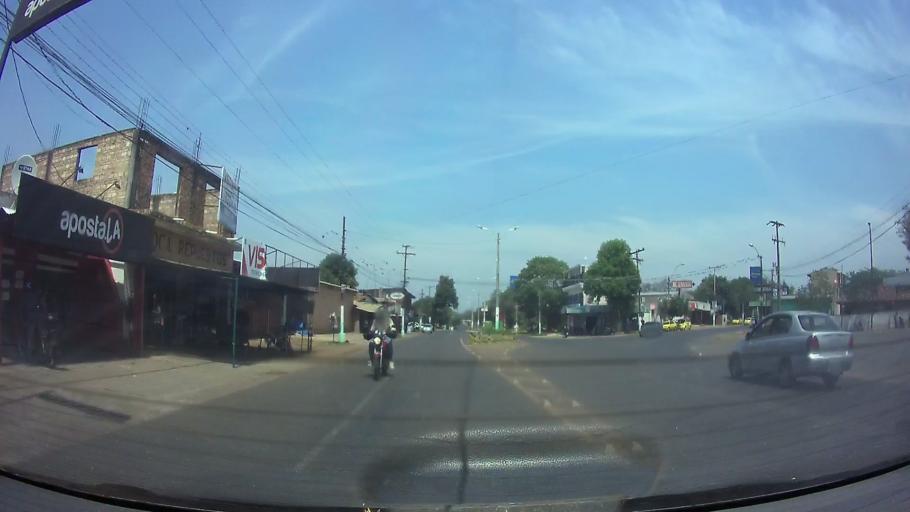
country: PY
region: Central
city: Guarambare
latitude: -25.4467
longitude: -57.4385
